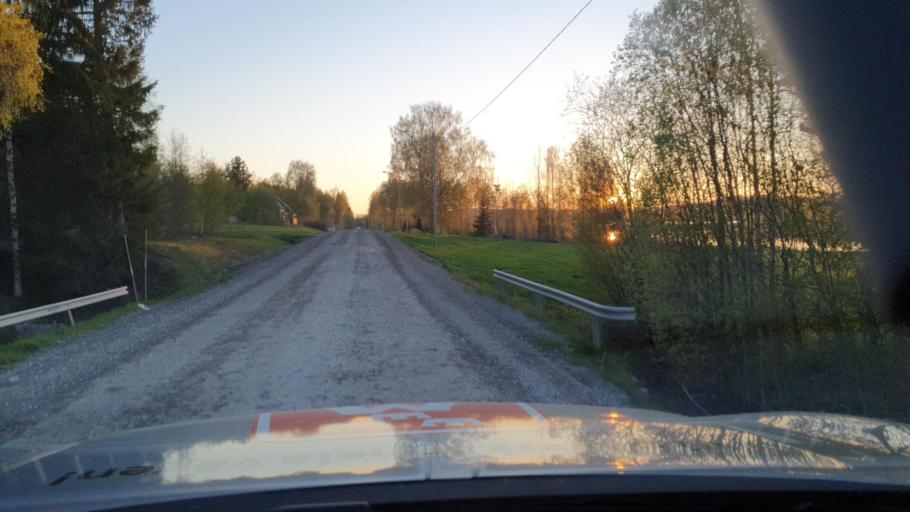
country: SE
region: Vaesternorrland
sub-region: OErnskoeldsviks Kommun
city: Bjasta
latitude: 63.5025
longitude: 18.4880
